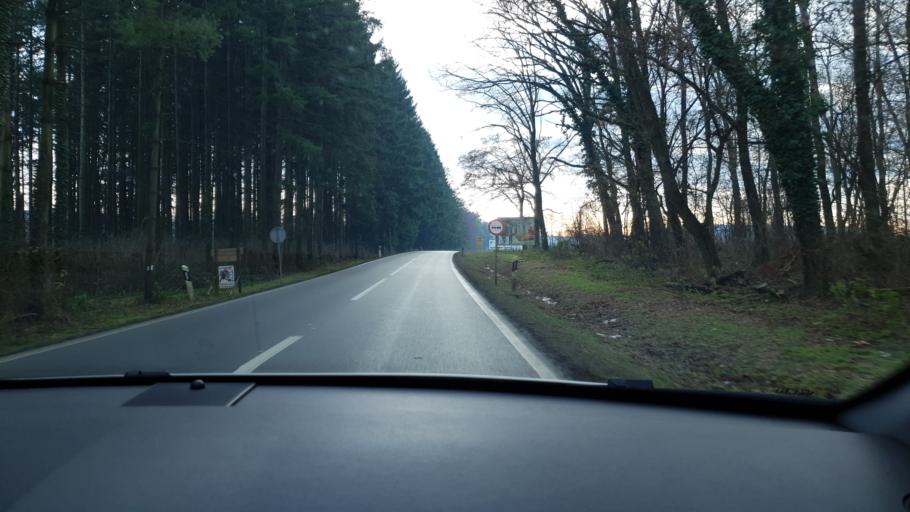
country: HR
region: Pozesko-Slavonska
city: Vidovci
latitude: 45.3493
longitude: 17.7207
